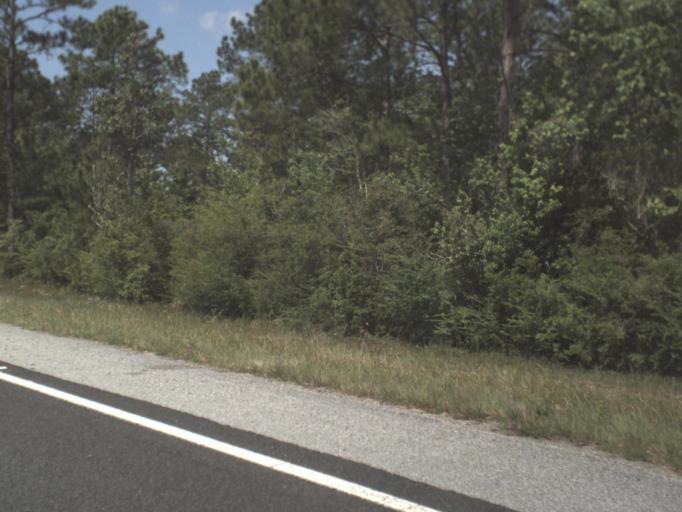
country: US
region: Florida
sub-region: Santa Rosa County
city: Bagdad
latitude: 30.5657
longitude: -87.0372
